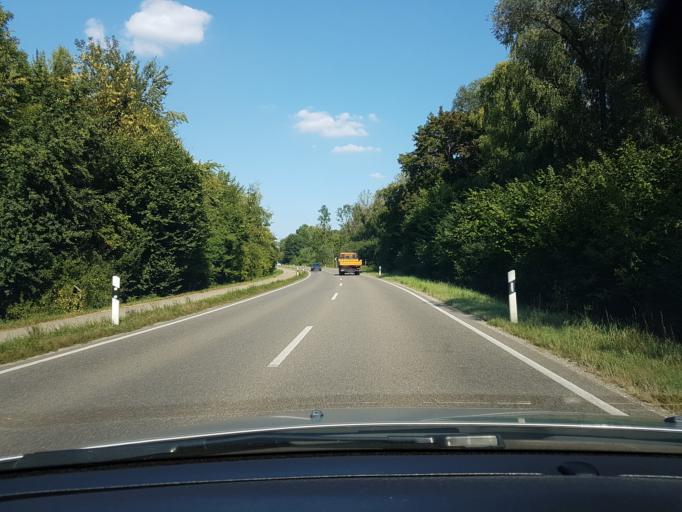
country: DE
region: Bavaria
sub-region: Swabia
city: Thierhaupten
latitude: 48.5617
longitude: 10.8783
